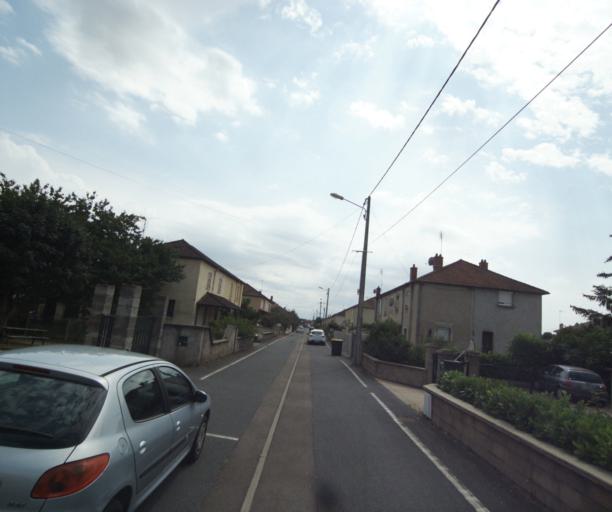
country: FR
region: Bourgogne
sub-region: Departement de Saone-et-Loire
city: Gueugnon
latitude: 46.6090
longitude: 4.0520
